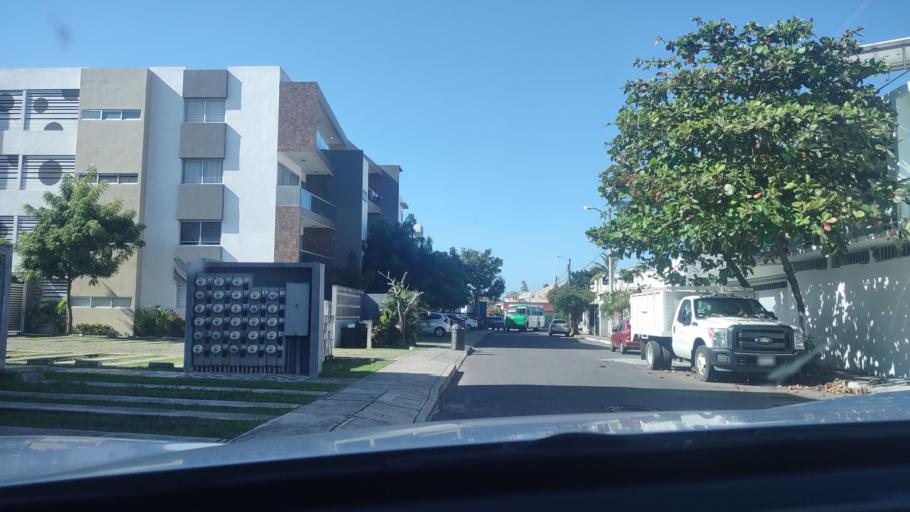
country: MX
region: Veracruz
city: Boca del Rio
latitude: 19.1085
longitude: -96.1125
